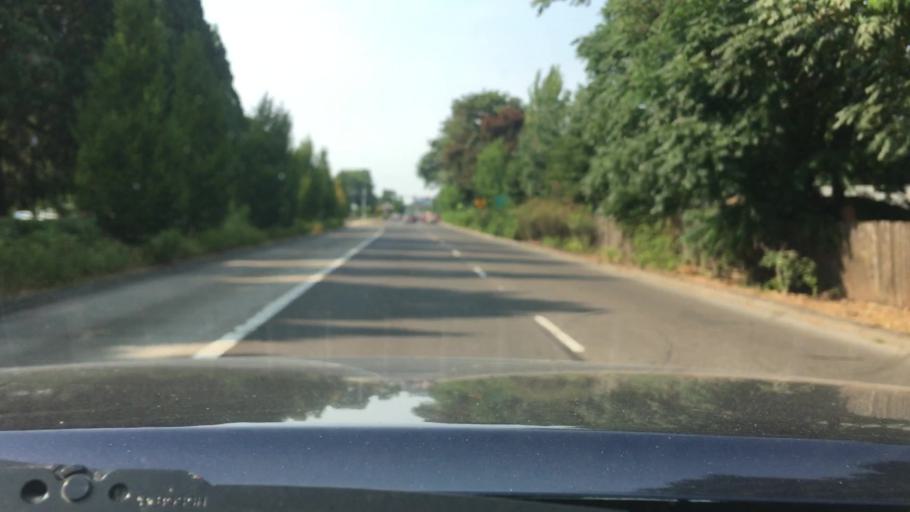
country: US
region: Oregon
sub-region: Lane County
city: Springfield
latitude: 44.0546
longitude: -123.0232
